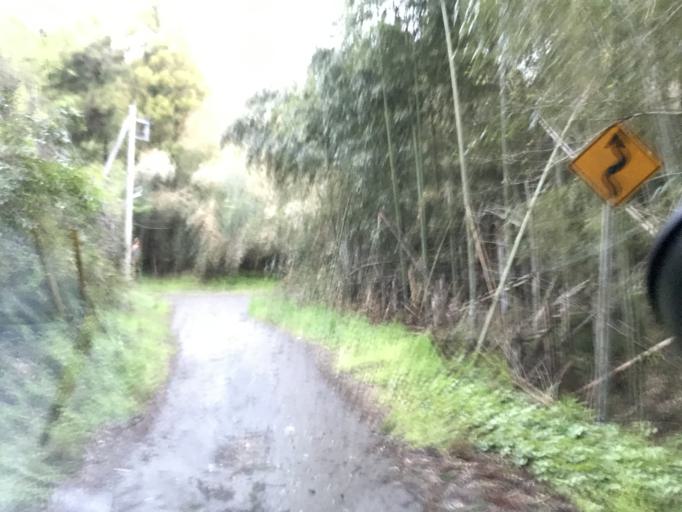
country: JP
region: Chiba
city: Sawara
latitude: 35.8289
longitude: 140.5000
